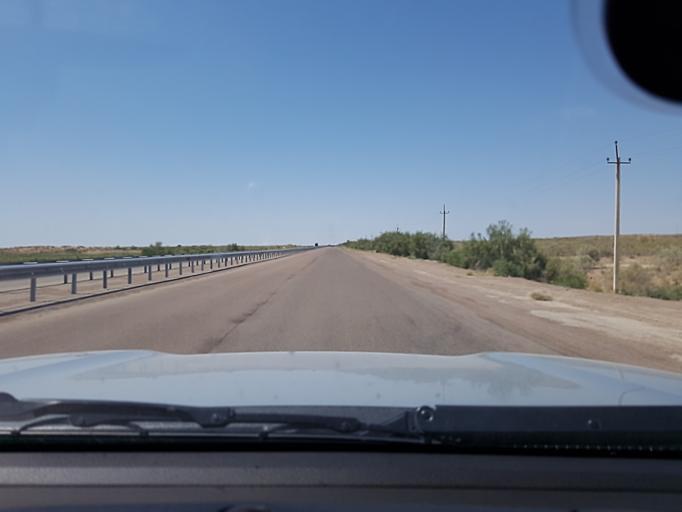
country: TM
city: Akdepe
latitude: 41.7510
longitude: 59.2777
